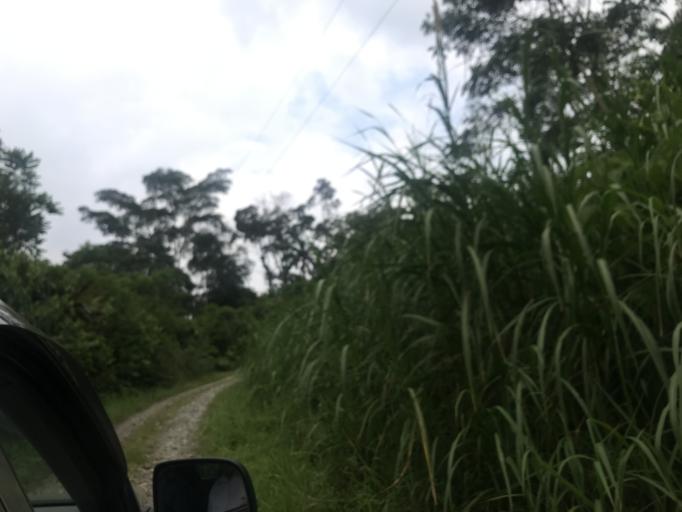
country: EC
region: Napo
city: Tena
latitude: -1.0215
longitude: -77.7420
